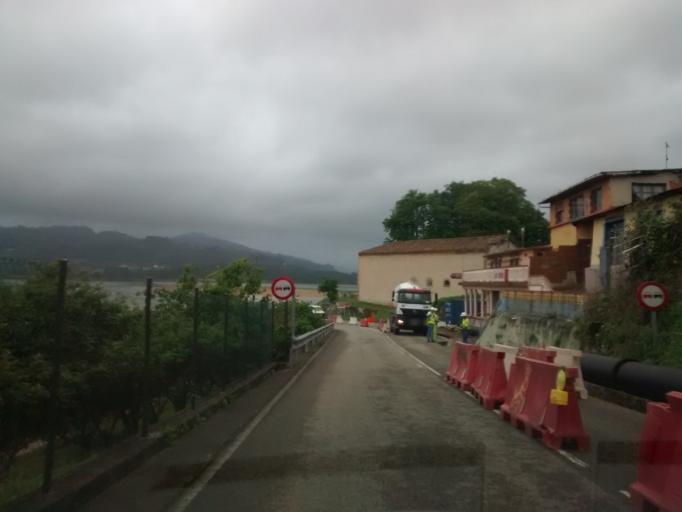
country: ES
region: Asturias
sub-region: Province of Asturias
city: Villaviciosa
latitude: 43.5252
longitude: -5.3923
